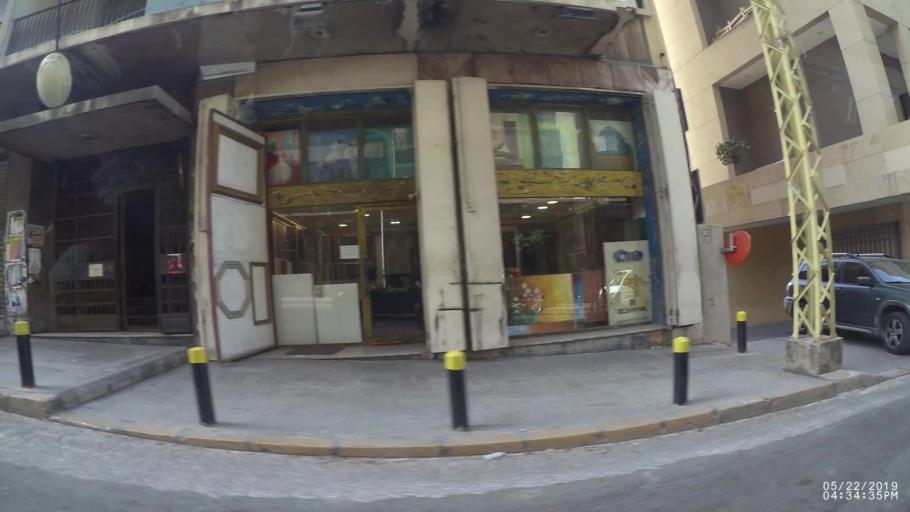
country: LB
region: Beyrouth
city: Beirut
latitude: 33.8960
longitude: 35.4938
